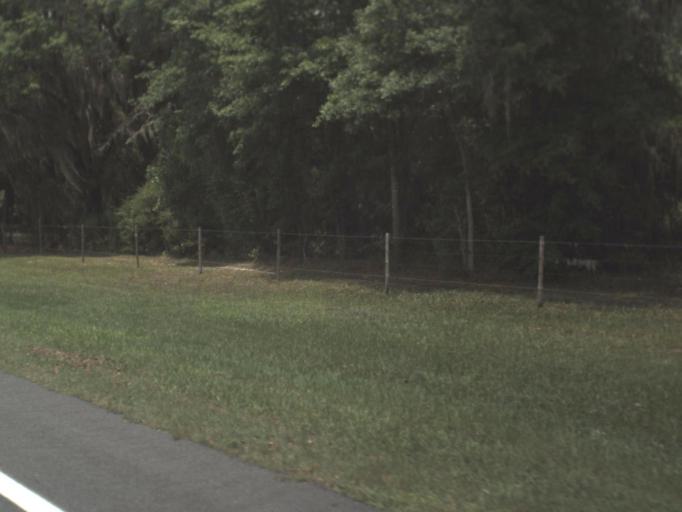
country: US
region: Florida
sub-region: Columbia County
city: Five Points
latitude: 30.4222
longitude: -82.6392
